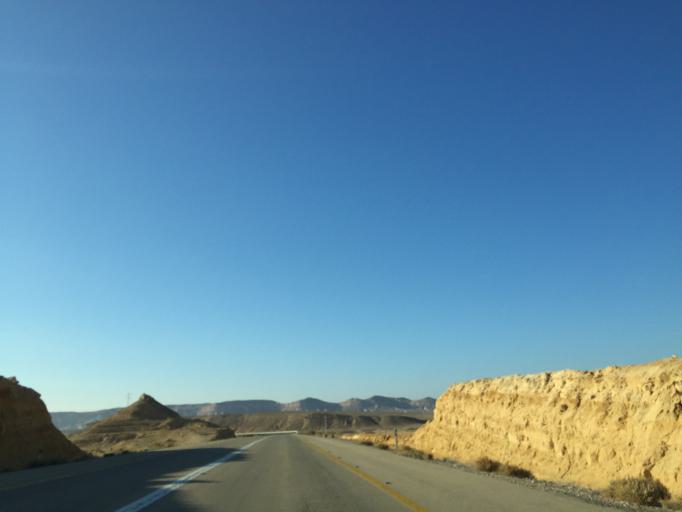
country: IL
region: Southern District
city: Mitzpe Ramon
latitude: 30.3068
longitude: 34.9677
